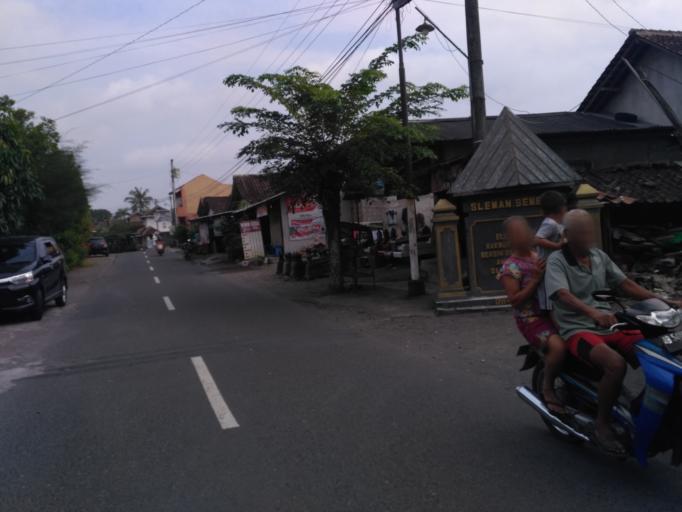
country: ID
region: Daerah Istimewa Yogyakarta
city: Melati
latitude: -7.7201
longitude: 110.4013
